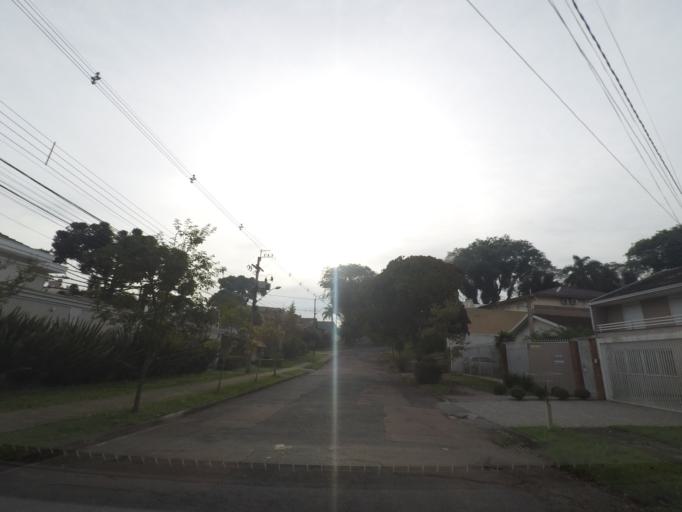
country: BR
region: Parana
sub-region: Curitiba
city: Curitiba
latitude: -25.4380
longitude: -49.2999
